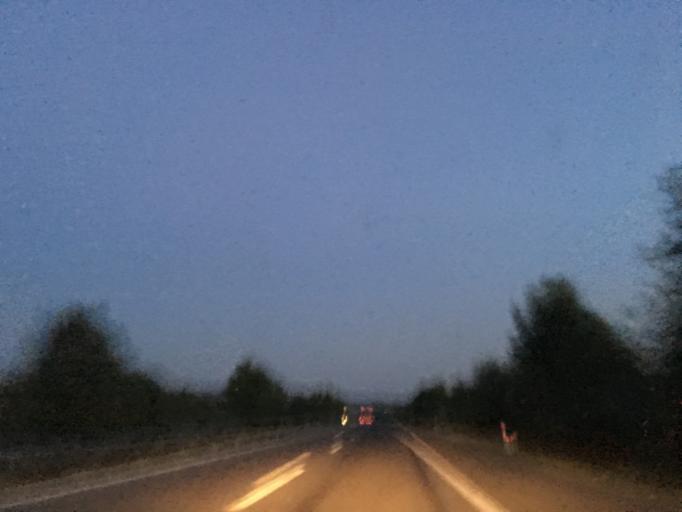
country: MK
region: Petrovec
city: Petrovec
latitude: 41.9145
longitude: 21.6424
